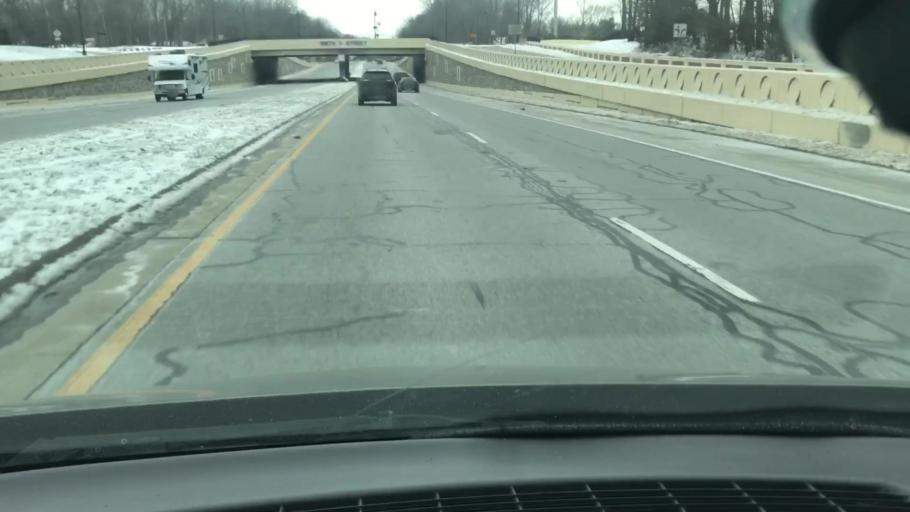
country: US
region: Indiana
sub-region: Hamilton County
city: Carmel
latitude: 39.9402
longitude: -86.1128
